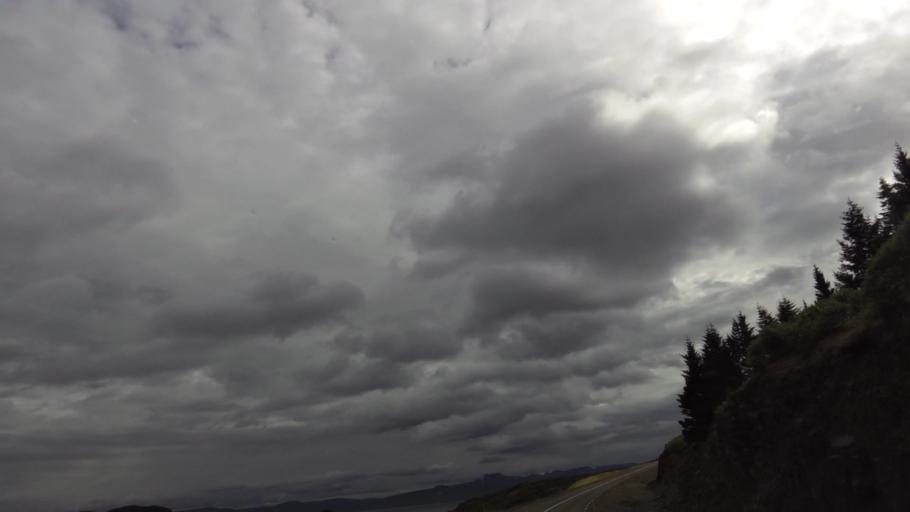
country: IS
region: West
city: Stykkisholmur
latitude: 65.5151
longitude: -22.1105
